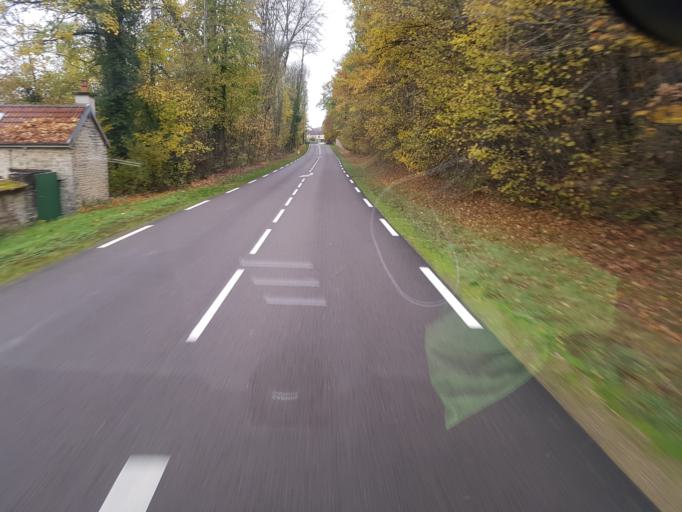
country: FR
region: Bourgogne
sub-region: Departement de la Cote-d'Or
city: Is-sur-Tille
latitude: 47.5406
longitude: 4.9755
